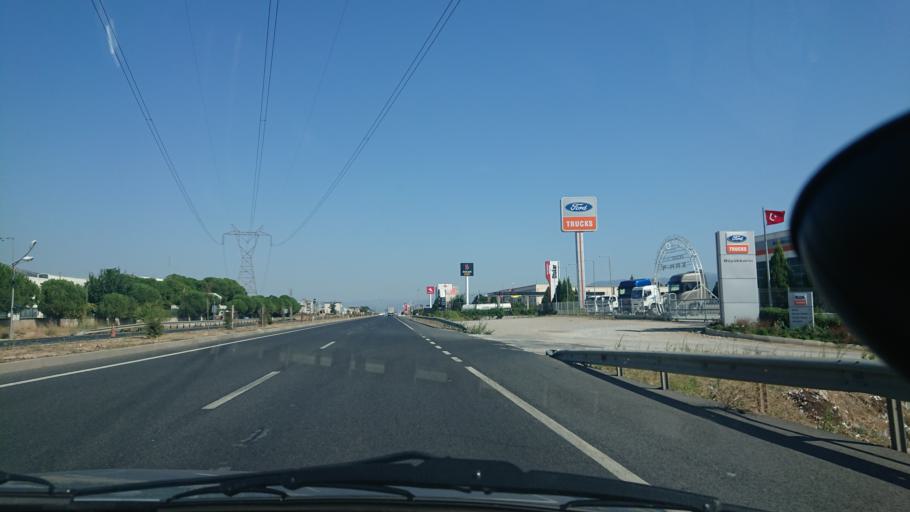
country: TR
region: Izmir
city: Kemalpasa
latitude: 38.4551
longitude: 27.4424
